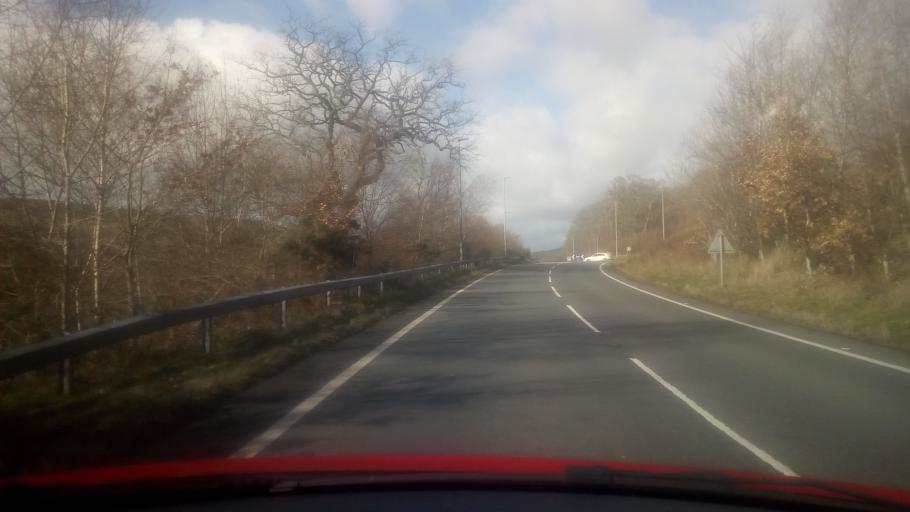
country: GB
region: Scotland
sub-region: The Scottish Borders
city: Selkirk
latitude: 55.6070
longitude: -2.8958
